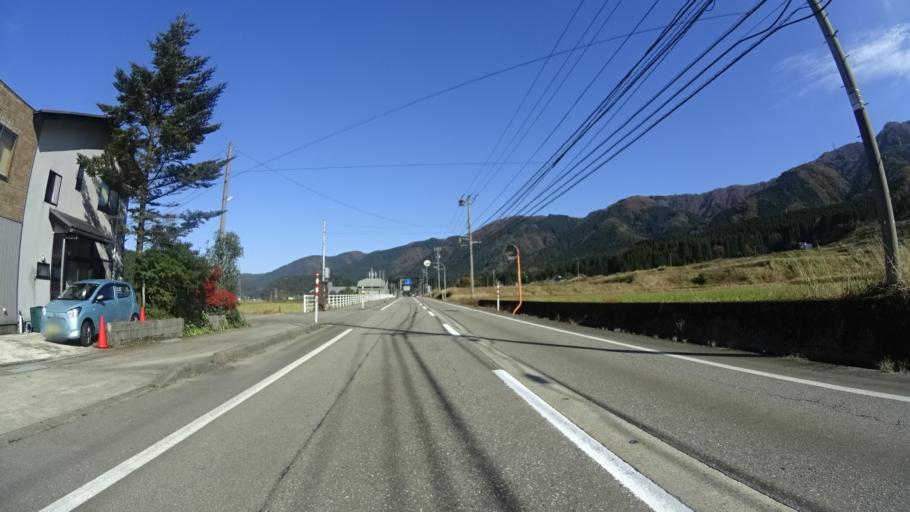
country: JP
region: Ishikawa
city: Tsurugi-asahimachi
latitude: 36.4250
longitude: 136.6322
